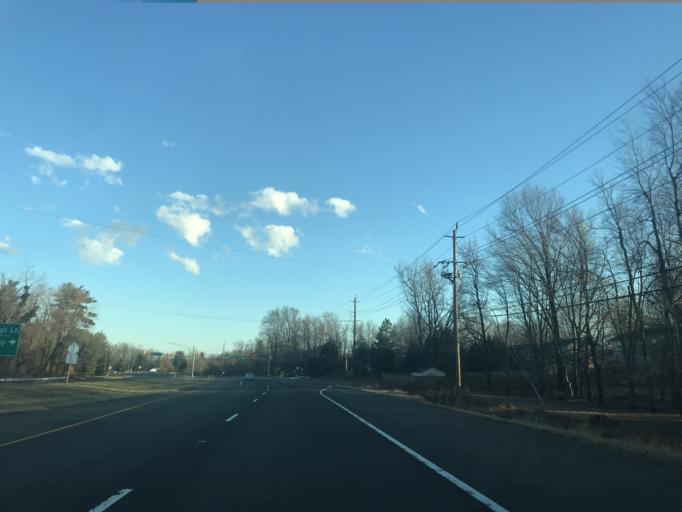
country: US
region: Maryland
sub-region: Prince George's County
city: Kettering
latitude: 38.8807
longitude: -76.8124
